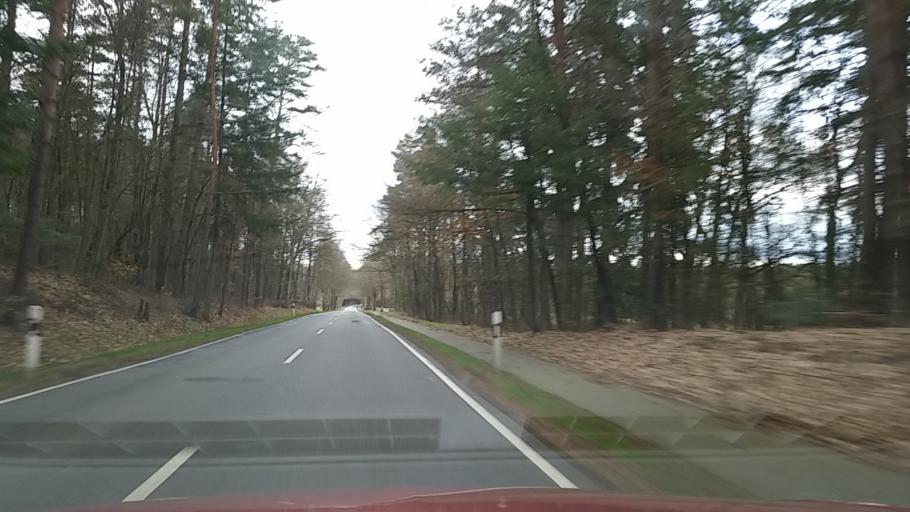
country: DE
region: Lower Saxony
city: Zernien
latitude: 53.1002
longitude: 10.9458
